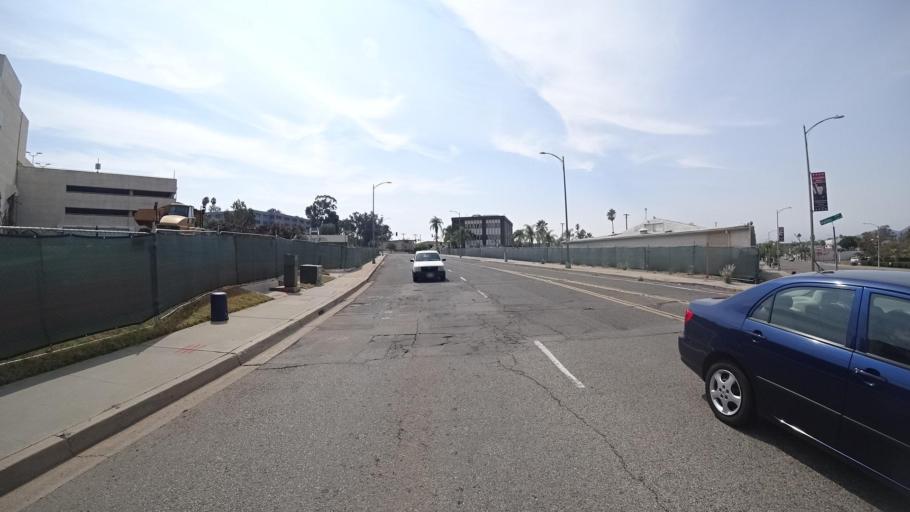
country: US
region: California
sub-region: San Diego County
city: Escondido
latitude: 33.1253
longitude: -117.0765
